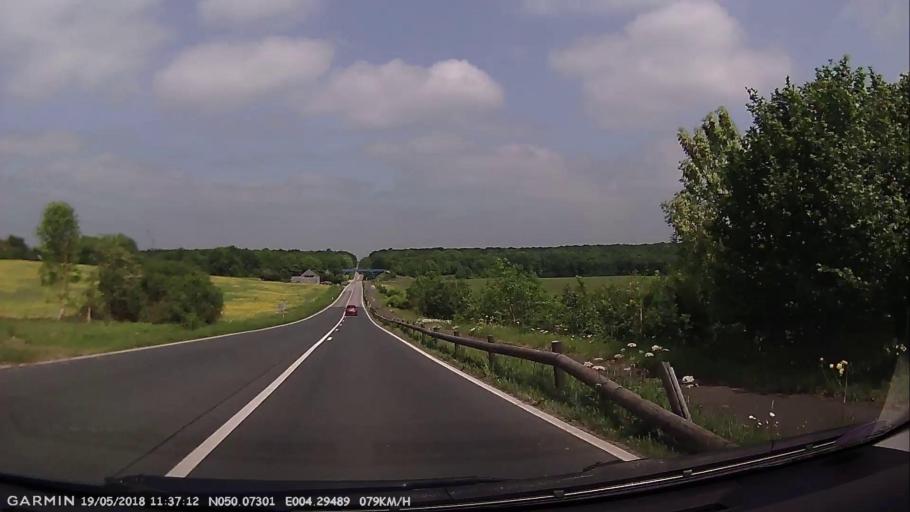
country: BE
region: Wallonia
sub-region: Province du Hainaut
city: Chimay
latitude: 50.0733
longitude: 4.2948
